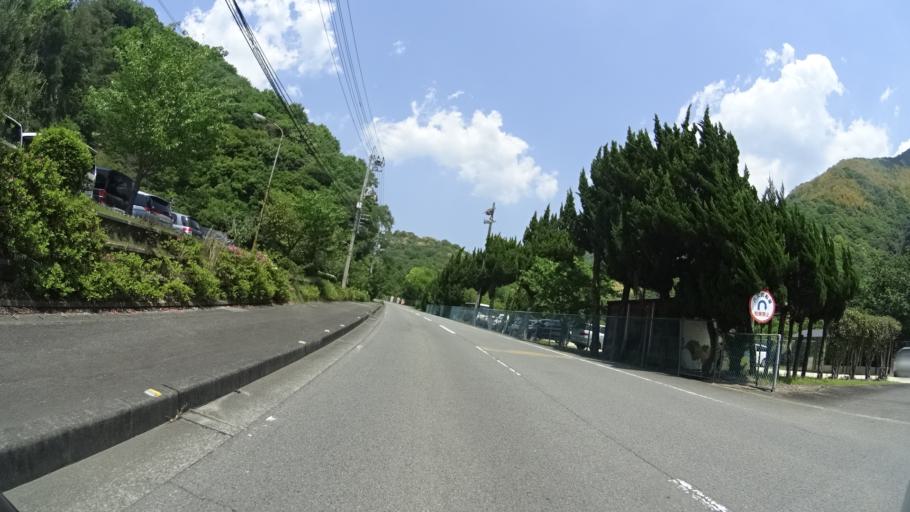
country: JP
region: Ehime
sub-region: Shikoku-chuo Shi
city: Matsuyama
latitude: 33.8668
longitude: 132.8263
